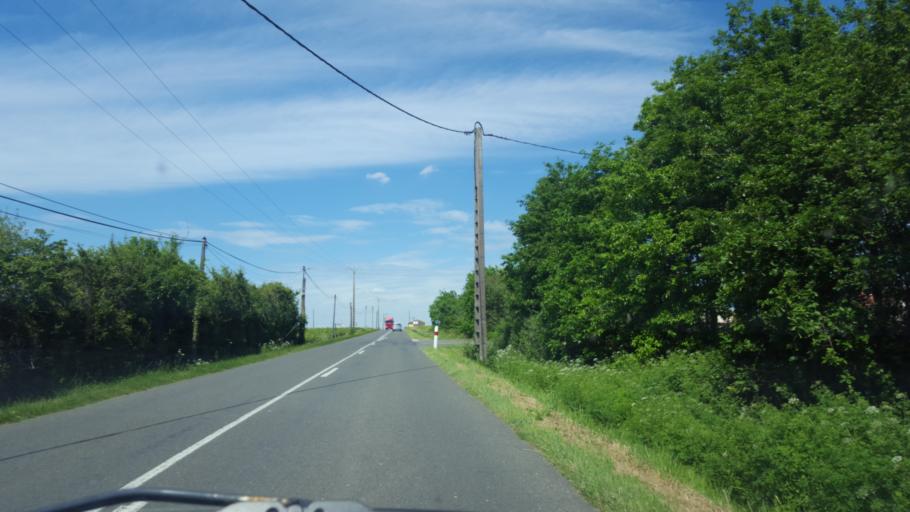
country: FR
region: Pays de la Loire
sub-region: Departement de la Loire-Atlantique
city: Saint-Philbert-de-Grand-Lieu
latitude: 47.0093
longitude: -1.6539
